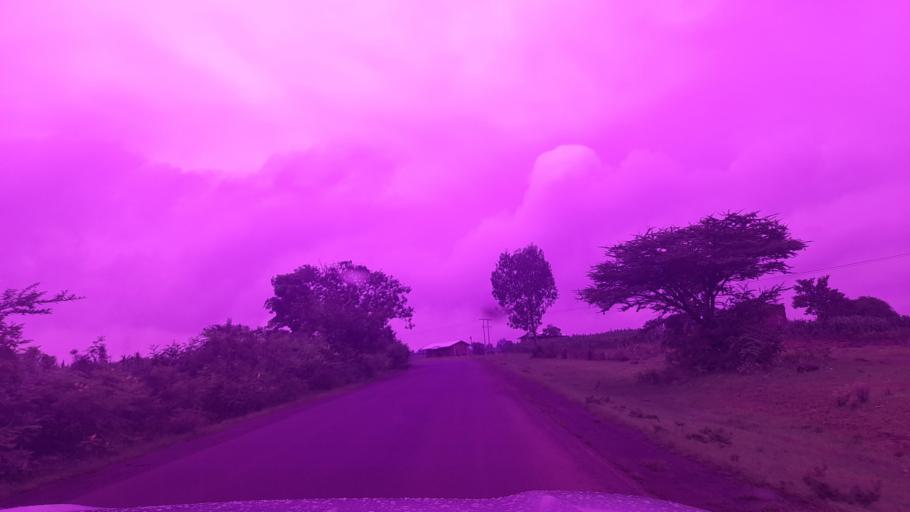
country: ET
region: Oromiya
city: Jima
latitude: 7.6899
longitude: 37.2311
